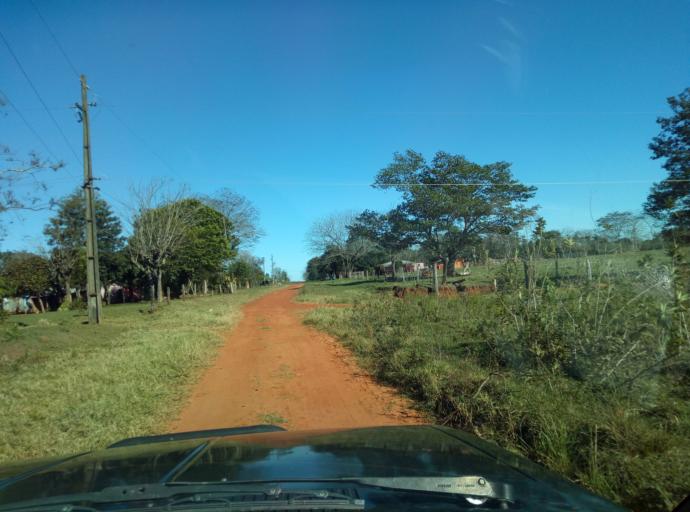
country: PY
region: Caaguazu
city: Doctor Cecilio Baez
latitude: -25.1789
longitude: -56.2420
